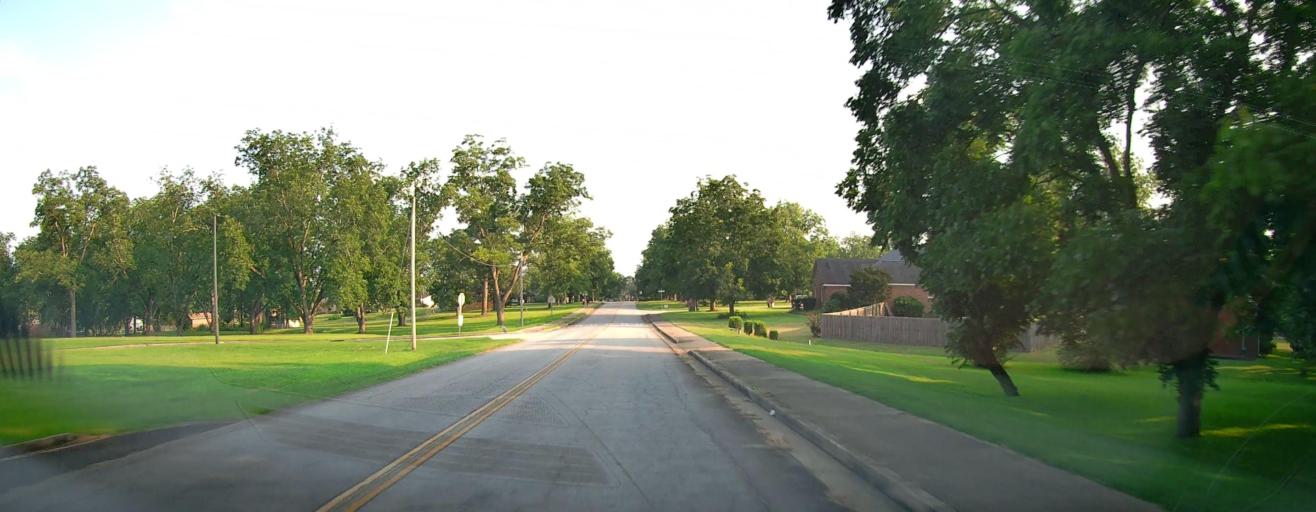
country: US
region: Georgia
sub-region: Peach County
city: Byron
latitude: 32.7374
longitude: -83.6939
